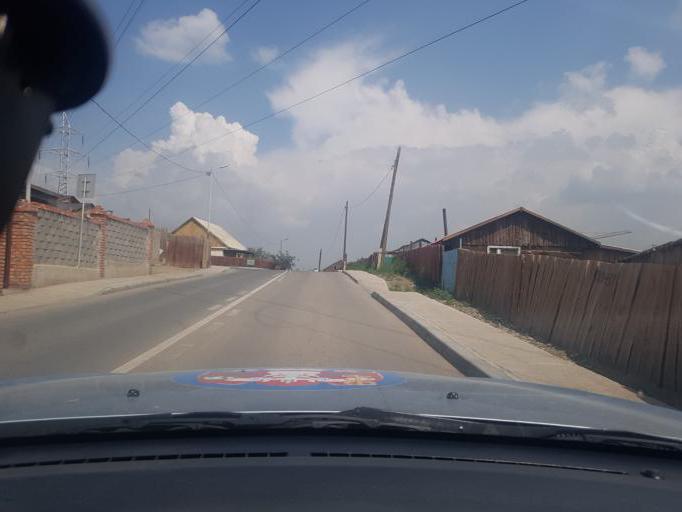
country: MN
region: Ulaanbaatar
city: Ulaanbaatar
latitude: 47.9365
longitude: 106.8972
